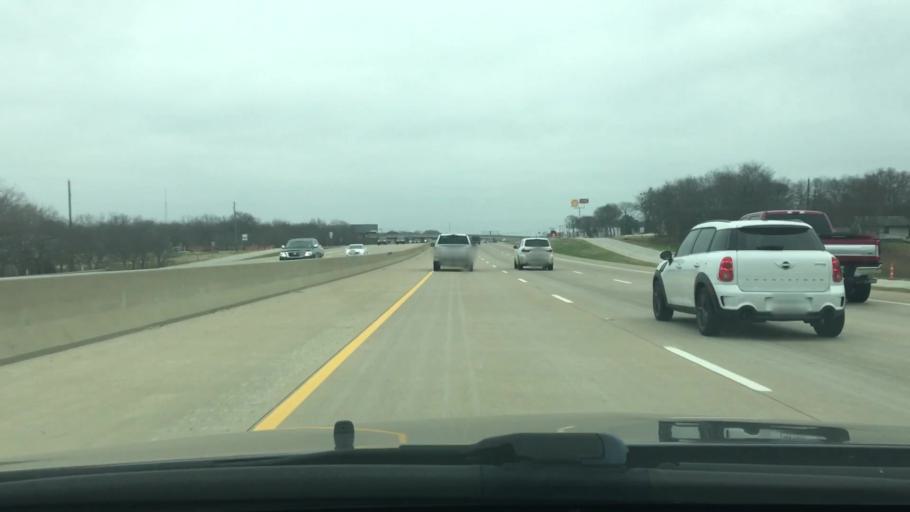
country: US
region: Texas
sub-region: Ellis County
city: Ennis
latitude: 32.2486
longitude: -96.4989
